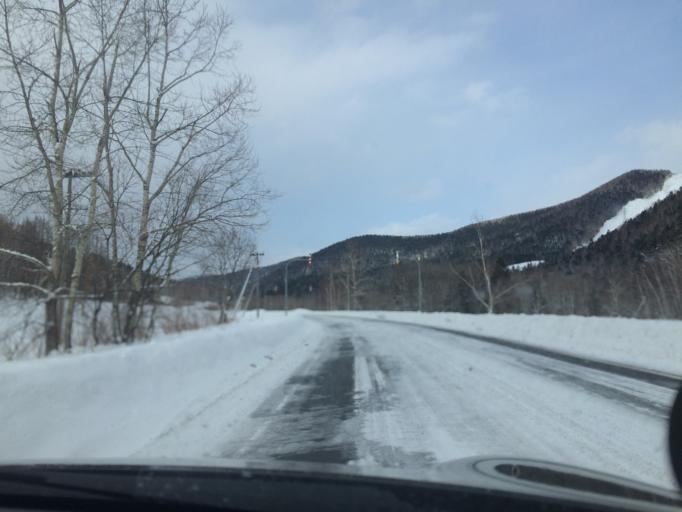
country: JP
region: Hokkaido
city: Shimo-furano
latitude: 43.0456
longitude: 142.5321
